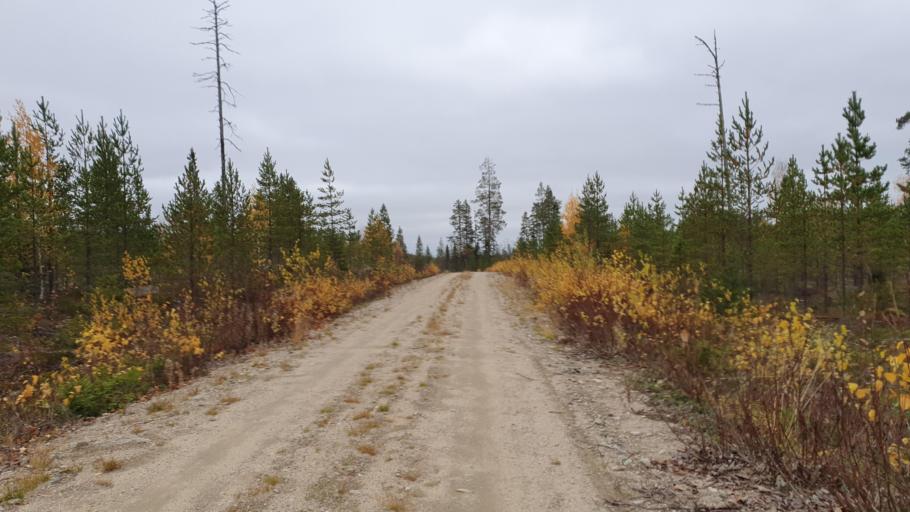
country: FI
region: Kainuu
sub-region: Kehys-Kainuu
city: Kuhmo
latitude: 64.4397
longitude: 29.6222
